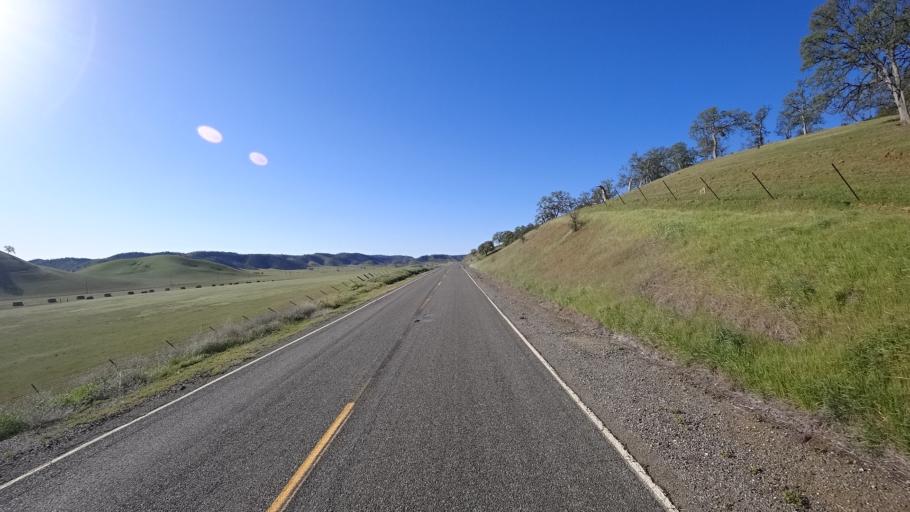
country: US
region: California
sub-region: Tehama County
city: Rancho Tehama Reserve
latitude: 39.7700
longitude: -122.5225
